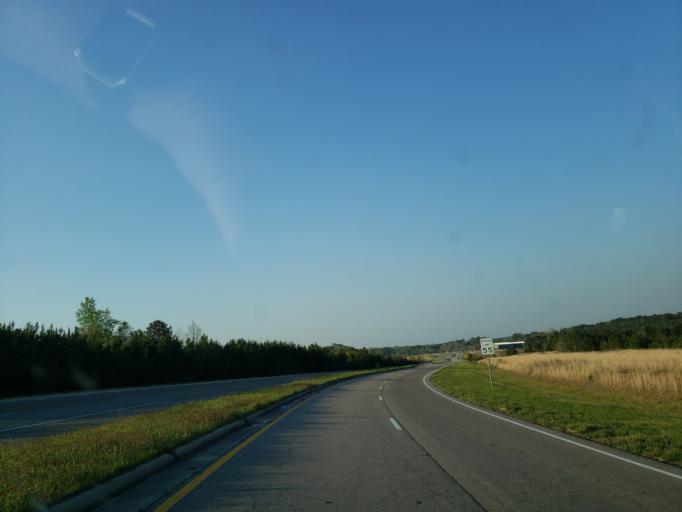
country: US
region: Mississippi
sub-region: Lauderdale County
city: Marion
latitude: 32.3821
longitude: -88.6555
